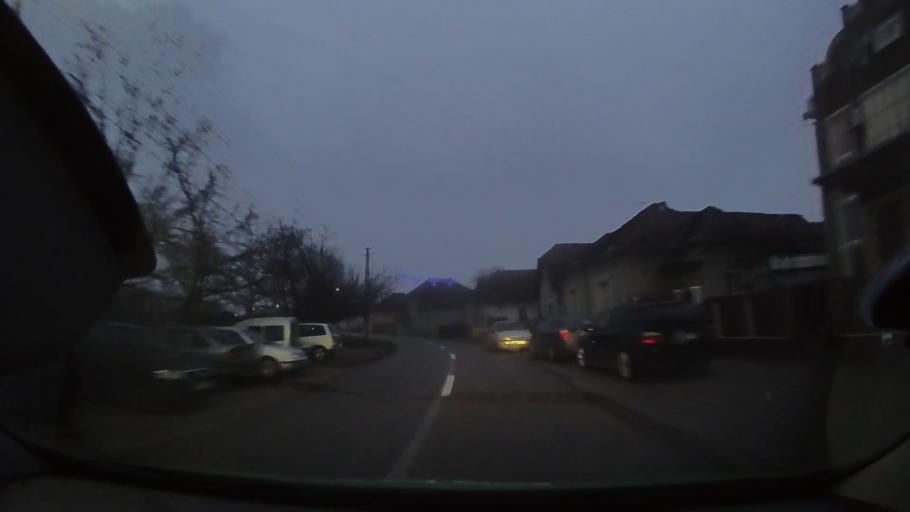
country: RO
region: Arad
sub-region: Comuna Archis
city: Archis
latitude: 46.4774
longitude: 22.0474
